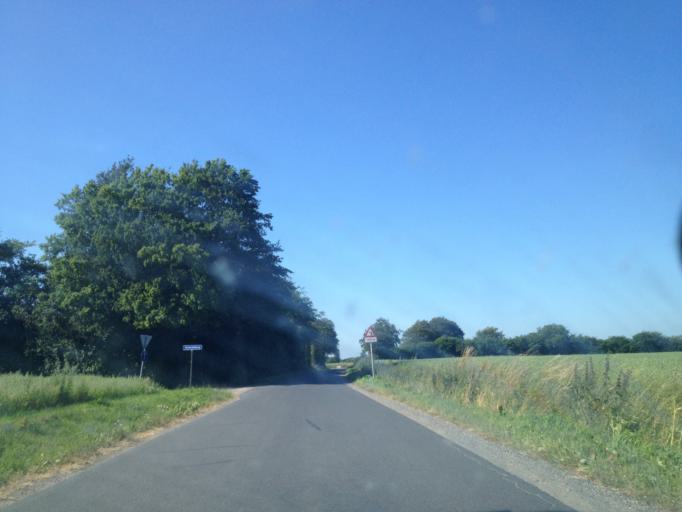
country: DK
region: South Denmark
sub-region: Kolding Kommune
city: Christiansfeld
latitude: 55.4024
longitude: 9.5172
